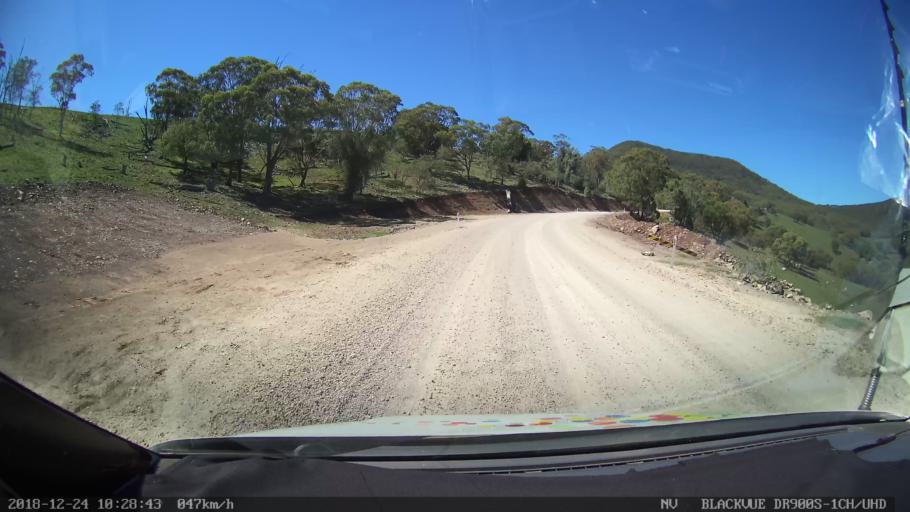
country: AU
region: New South Wales
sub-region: Liverpool Plains
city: Quirindi
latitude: -31.8278
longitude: 150.5316
